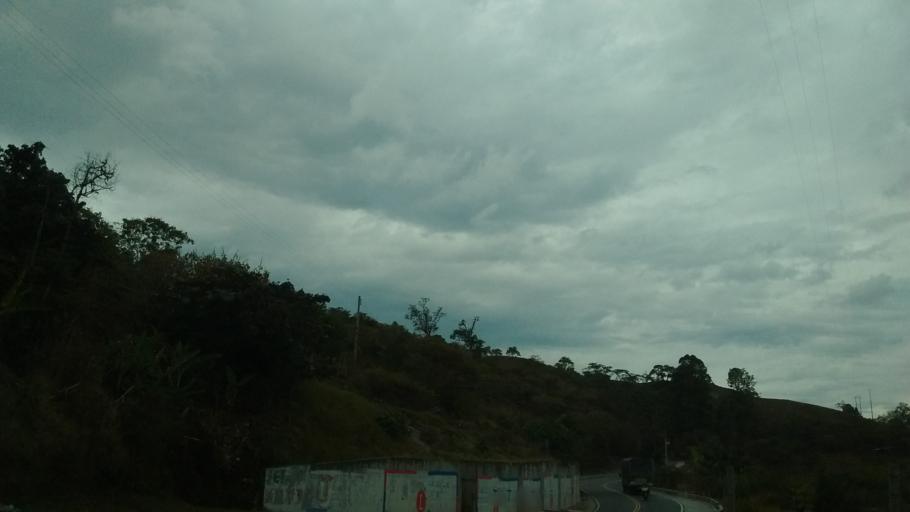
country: CO
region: Cauca
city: Rosas
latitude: 2.2671
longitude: -76.7344
